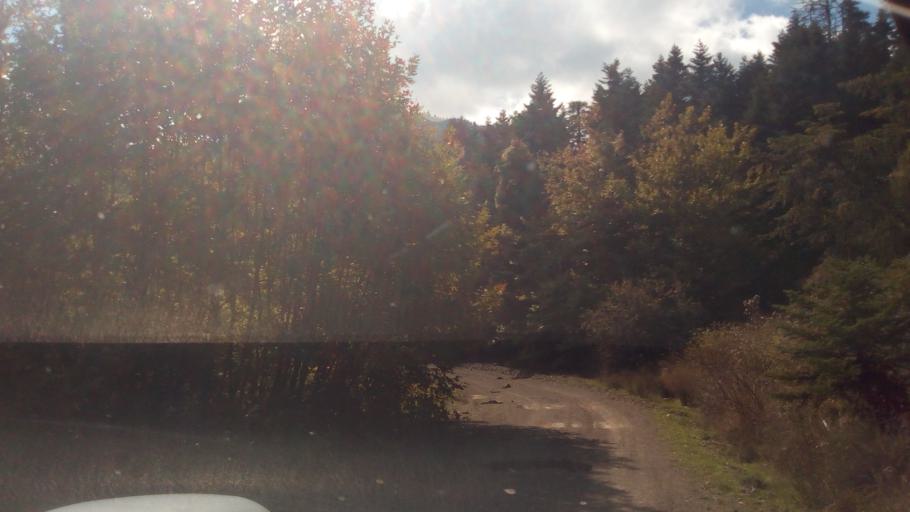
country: GR
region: Central Greece
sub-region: Nomos Fokidos
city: Lidoriki
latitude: 38.6422
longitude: 21.9545
